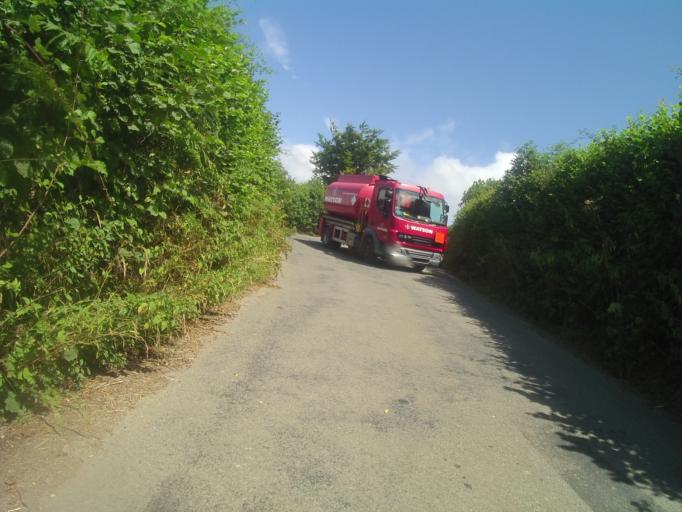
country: GB
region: England
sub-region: Devon
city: Buckfastleigh
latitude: 50.5086
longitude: -3.8180
